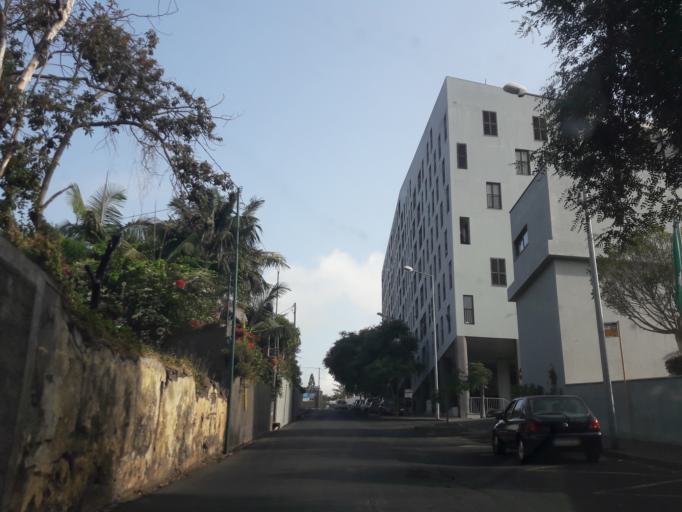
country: PT
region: Madeira
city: Camara de Lobos
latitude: 32.6489
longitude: -16.9416
